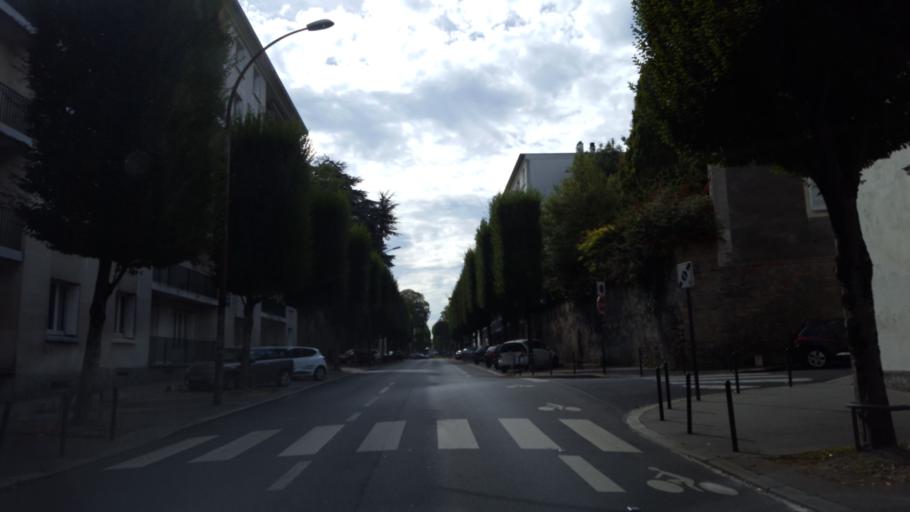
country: FR
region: Pays de la Loire
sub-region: Departement de la Loire-Atlantique
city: Nantes
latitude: 47.2130
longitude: -1.5754
